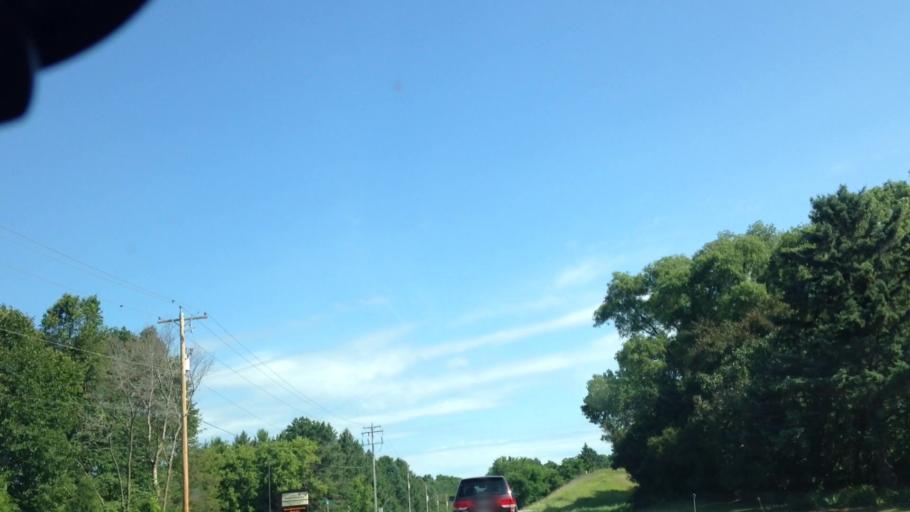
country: US
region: Wisconsin
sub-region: Washington County
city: West Bend
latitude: 43.3935
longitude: -88.2408
